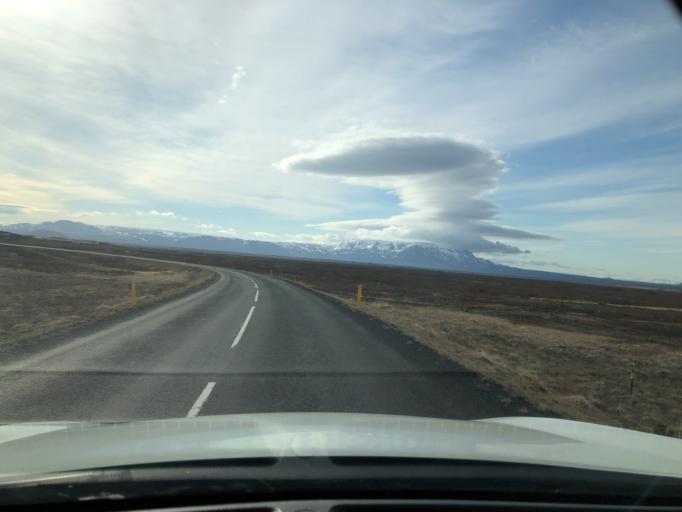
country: IS
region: Northeast
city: Laugar
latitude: 65.5721
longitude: -17.0842
